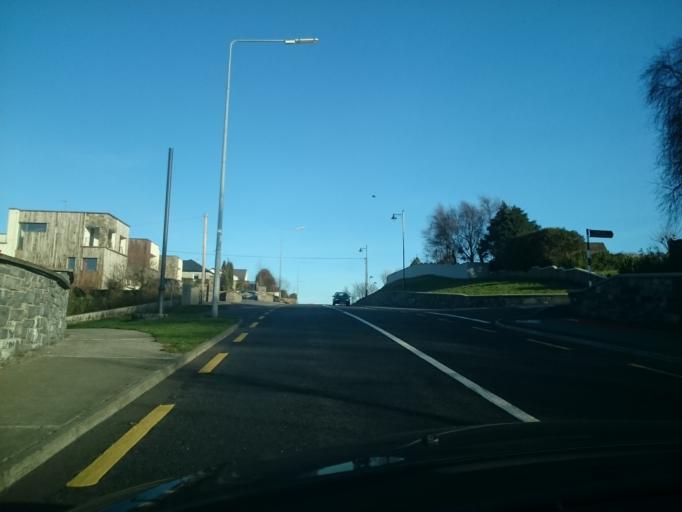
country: IE
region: Connaught
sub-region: Maigh Eo
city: Westport
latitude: 53.8060
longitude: -9.5248
